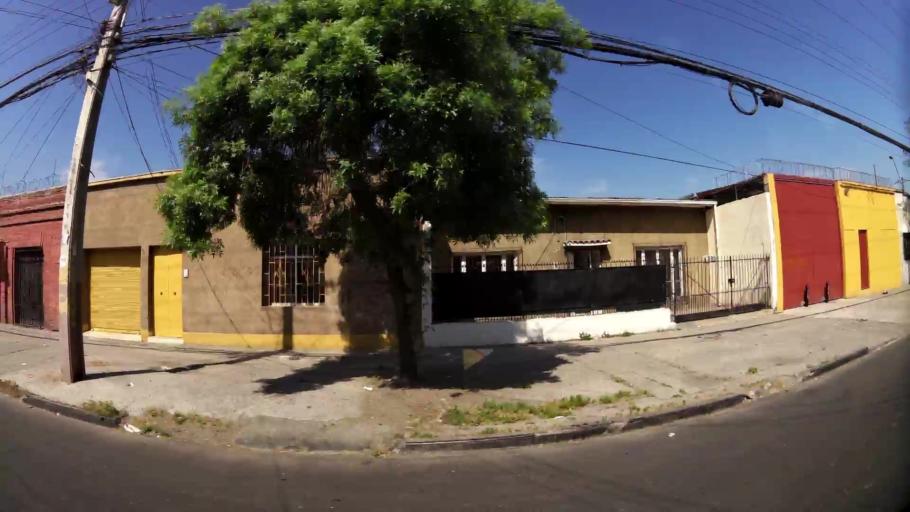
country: CL
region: Santiago Metropolitan
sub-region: Provincia de Santiago
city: Santiago
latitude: -33.4082
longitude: -70.6448
